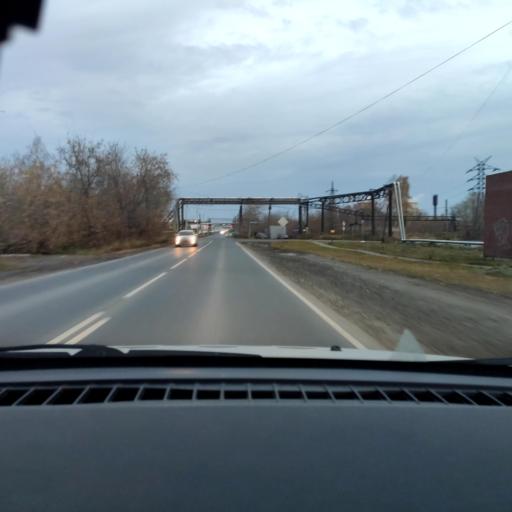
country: RU
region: Perm
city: Gamovo
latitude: 57.9123
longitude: 56.1583
